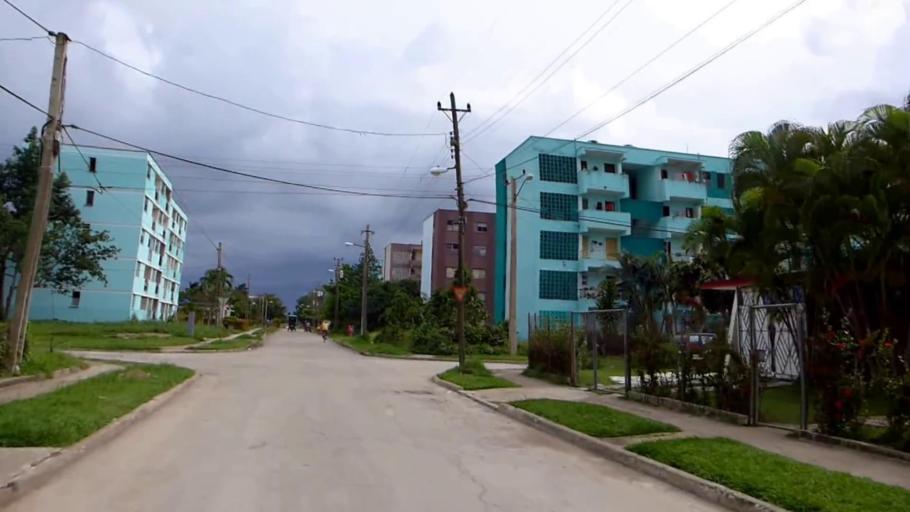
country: CU
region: Camaguey
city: Camaguey
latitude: 21.3641
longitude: -77.8945
